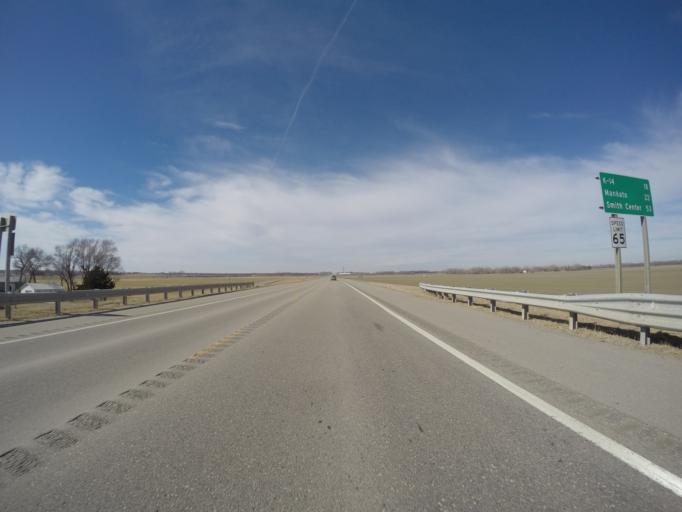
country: US
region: Kansas
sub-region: Republic County
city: Belleville
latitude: 39.7988
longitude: -97.7931
